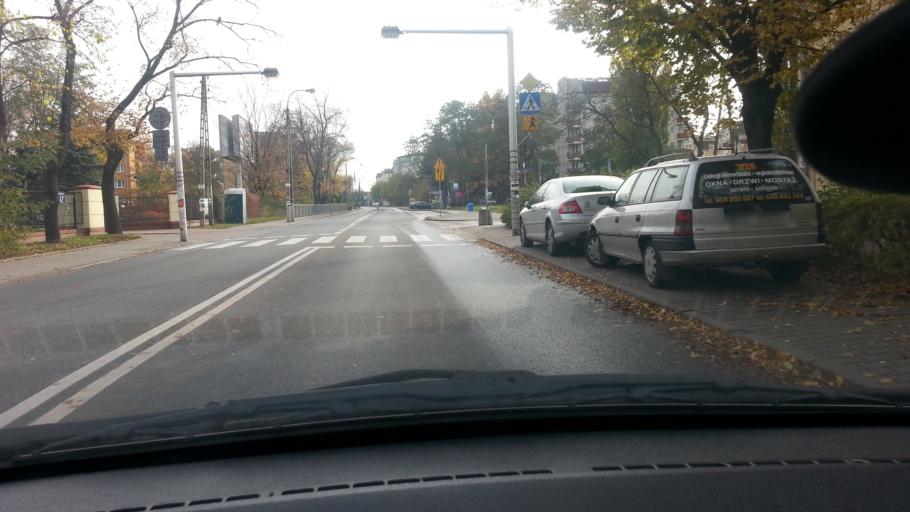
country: PL
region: Masovian Voivodeship
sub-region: Warszawa
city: Ursus
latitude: 52.1954
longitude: 20.8985
